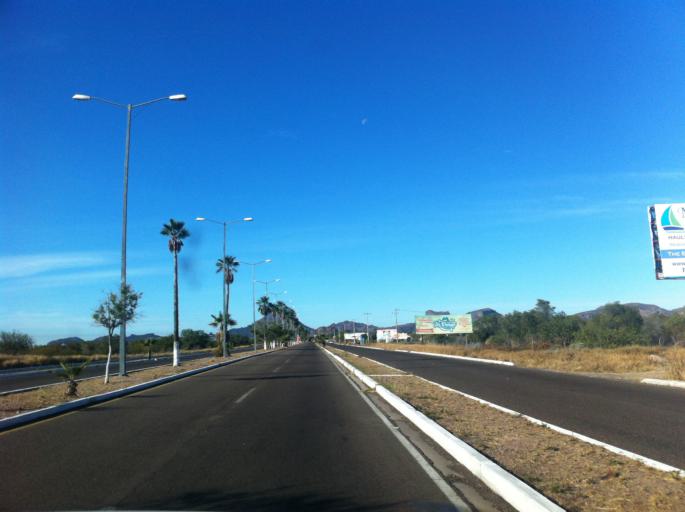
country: MX
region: Sonora
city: Heroica Guaymas
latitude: 27.9710
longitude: -110.9977
